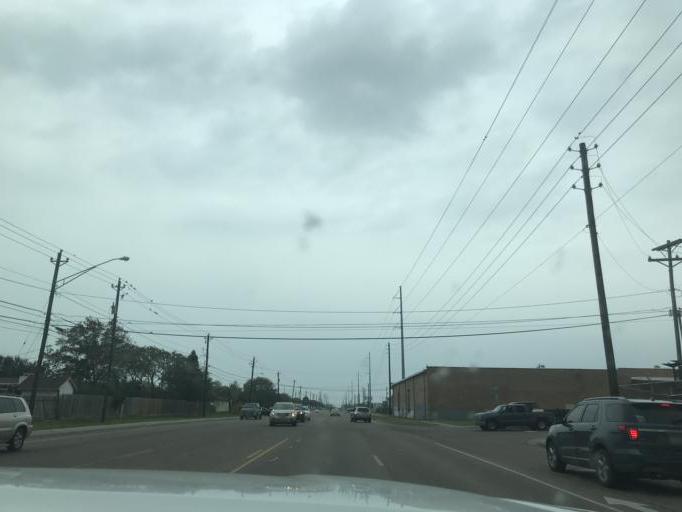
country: US
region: Texas
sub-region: Nueces County
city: Corpus Christi
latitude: 27.6953
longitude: -97.3700
